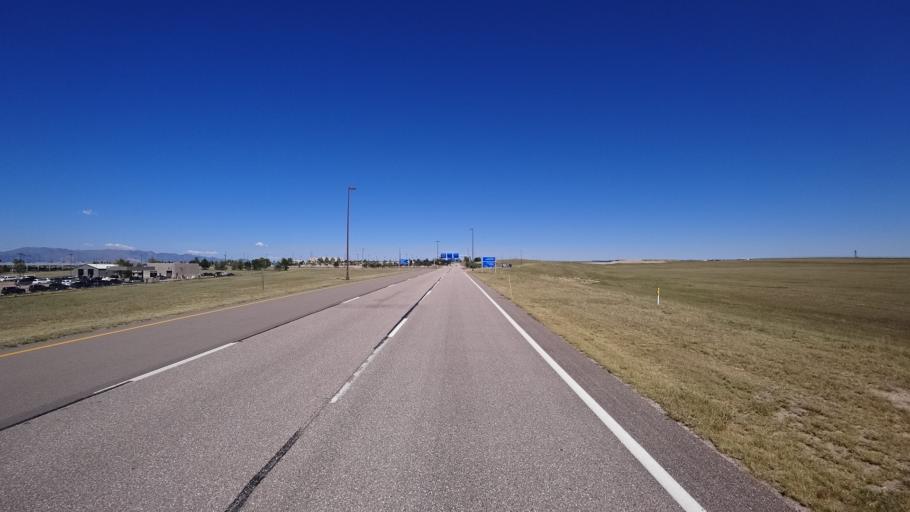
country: US
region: Colorado
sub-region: El Paso County
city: Security-Widefield
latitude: 38.7901
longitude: -104.6974
